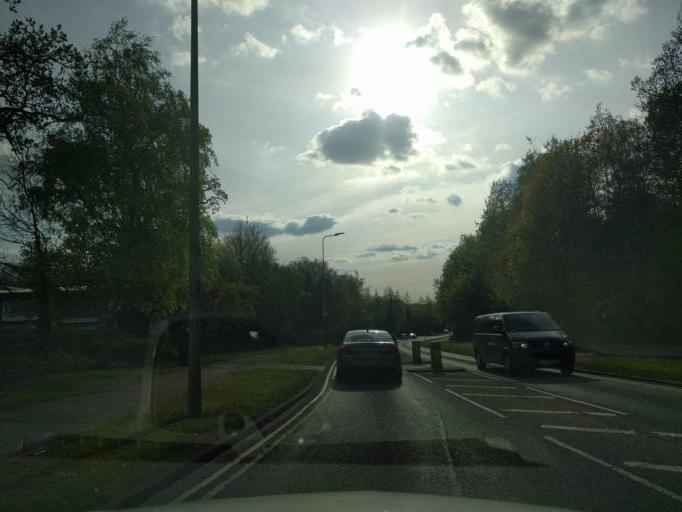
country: GB
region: England
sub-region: Suffolk
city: Bury St Edmunds
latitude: 52.2402
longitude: 0.7411
